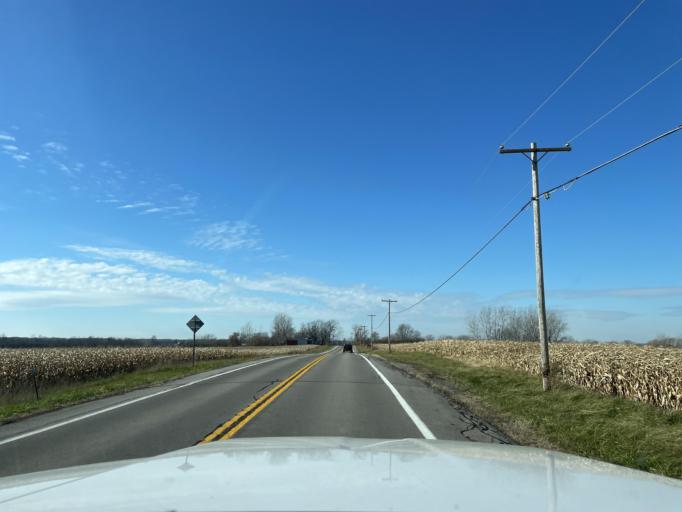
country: US
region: New York
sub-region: Niagara County
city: Middleport
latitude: 43.2157
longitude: -78.4530
